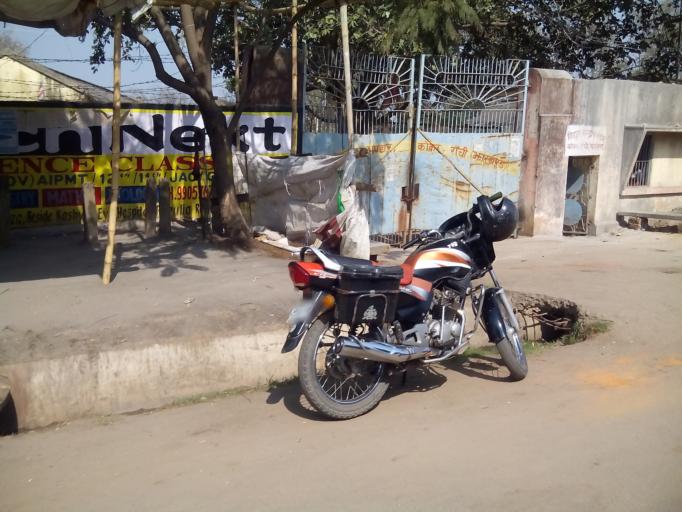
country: IN
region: Jharkhand
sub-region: Ranchi
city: Ranchi
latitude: 23.3767
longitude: 85.3561
